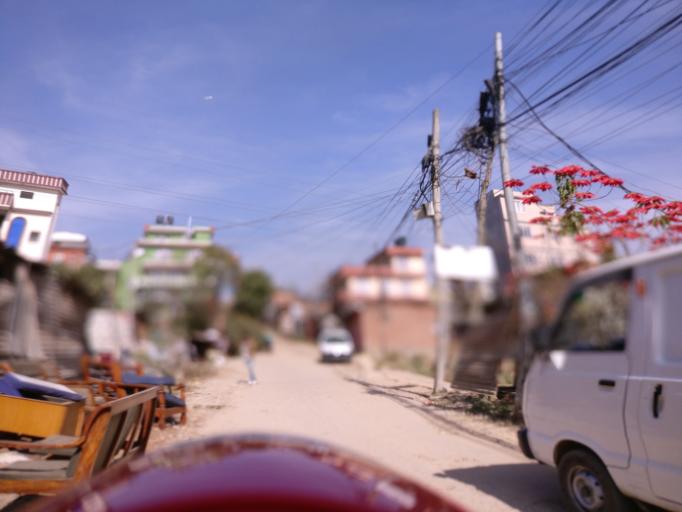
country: NP
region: Central Region
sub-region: Bagmati Zone
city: Patan
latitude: 27.6655
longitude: 85.3076
